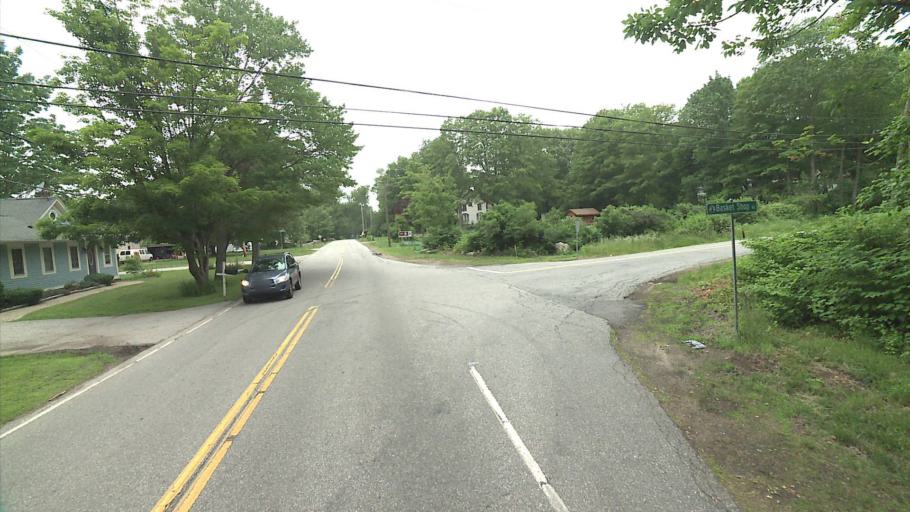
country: US
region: Connecticut
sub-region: Tolland County
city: Hebron
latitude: 41.6862
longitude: -72.3609
